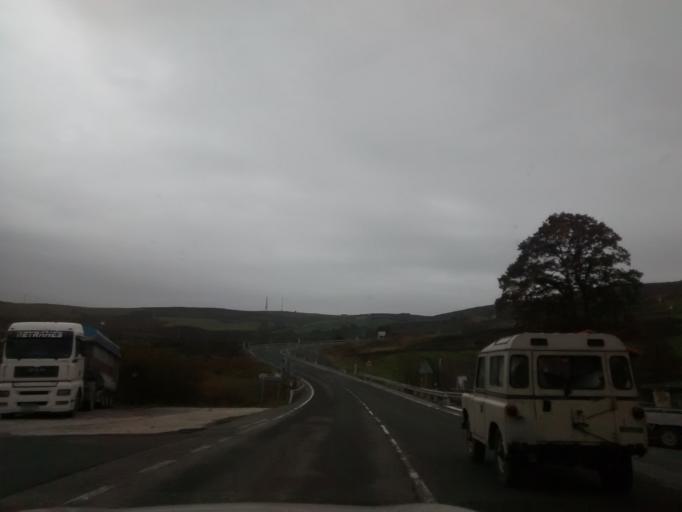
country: ES
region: Cantabria
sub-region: Provincia de Cantabria
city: San Pedro del Romeral
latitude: 43.0655
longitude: -3.8852
